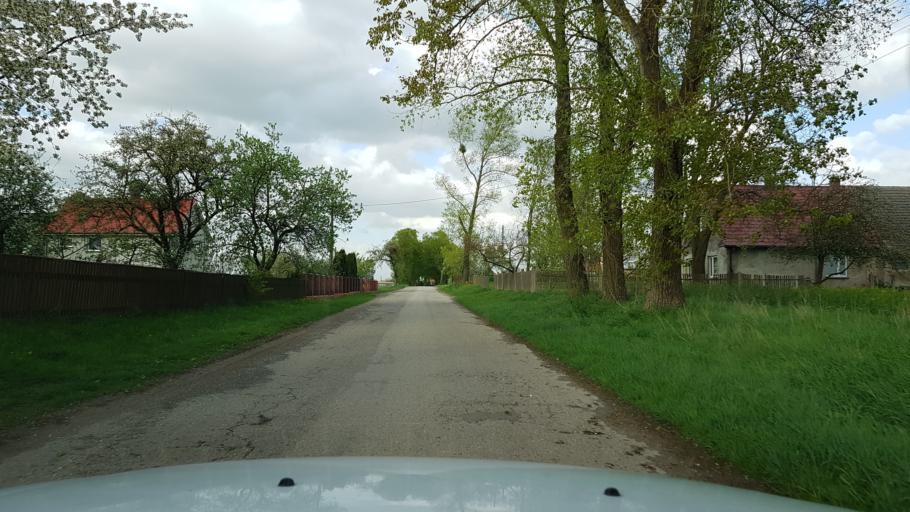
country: PL
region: West Pomeranian Voivodeship
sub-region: Powiat pyrzycki
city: Przelewice
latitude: 53.0491
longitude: 15.0995
